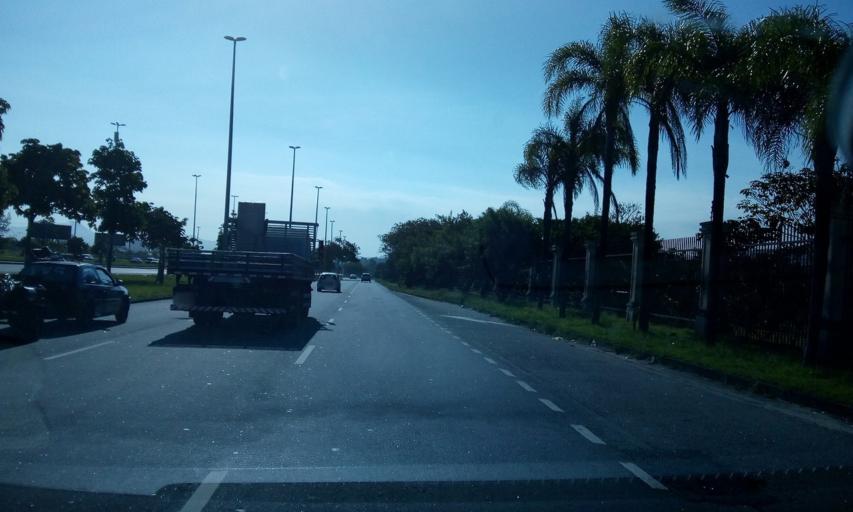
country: BR
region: Rio de Janeiro
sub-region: Nilopolis
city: Nilopolis
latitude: -22.9998
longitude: -43.4005
